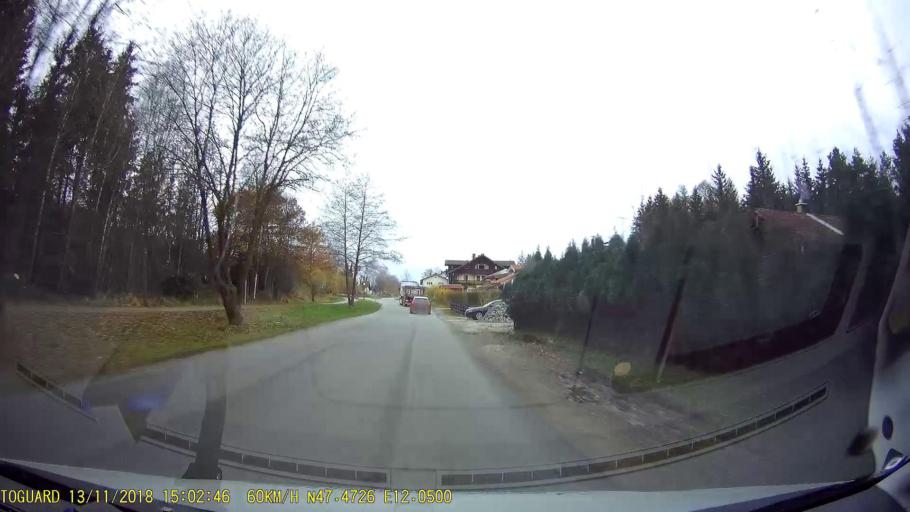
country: DE
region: Bavaria
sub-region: Upper Bavaria
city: Raubling
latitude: 47.7879
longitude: 12.0829
